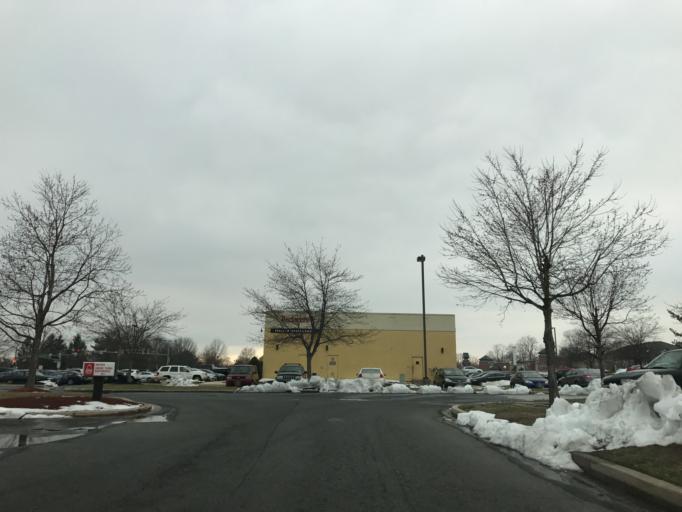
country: US
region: Maryland
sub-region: Harford County
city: Bel Air South
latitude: 39.4980
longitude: -76.3282
